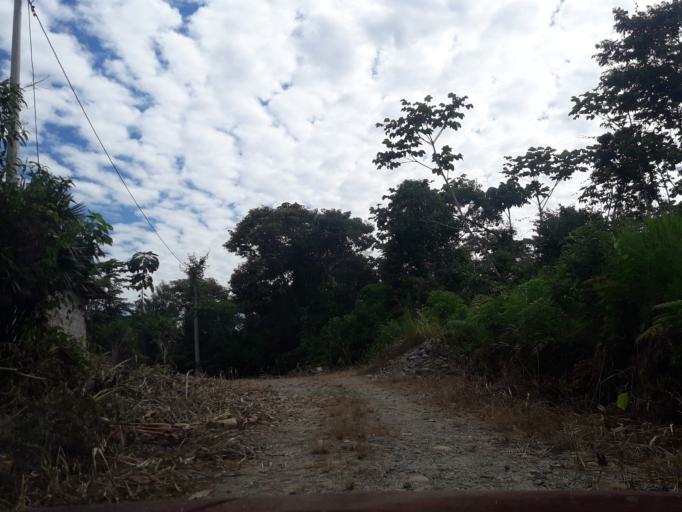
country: EC
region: Napo
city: Tena
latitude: -0.9824
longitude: -77.8210
